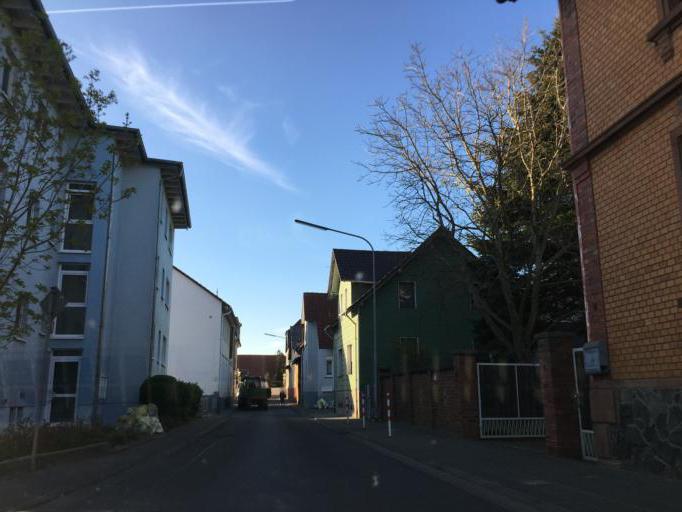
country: DE
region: Hesse
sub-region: Regierungsbezirk Darmstadt
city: Rossdorf
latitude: 49.8695
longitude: 8.7877
